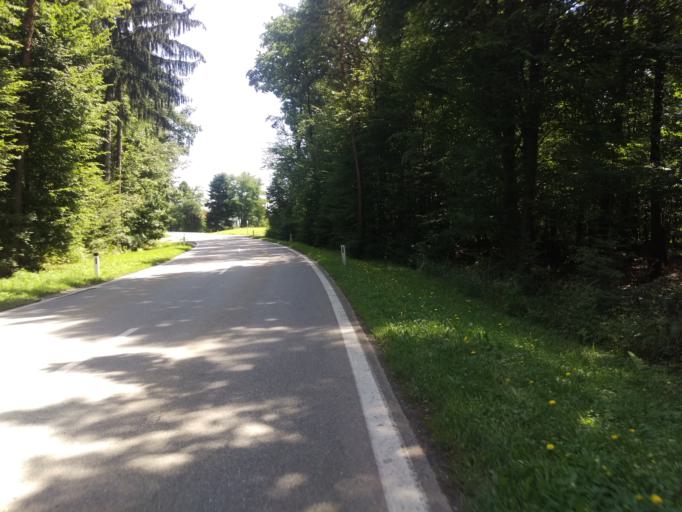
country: AT
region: Styria
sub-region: Politischer Bezirk Graz-Umgebung
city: Zettling
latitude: 46.9694
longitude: 15.4414
